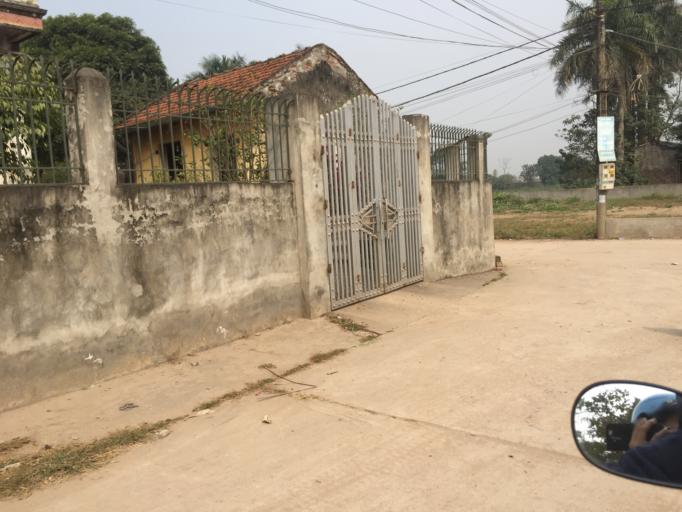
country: VN
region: Hung Yen
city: Van Giang
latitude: 20.9459
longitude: 105.9112
